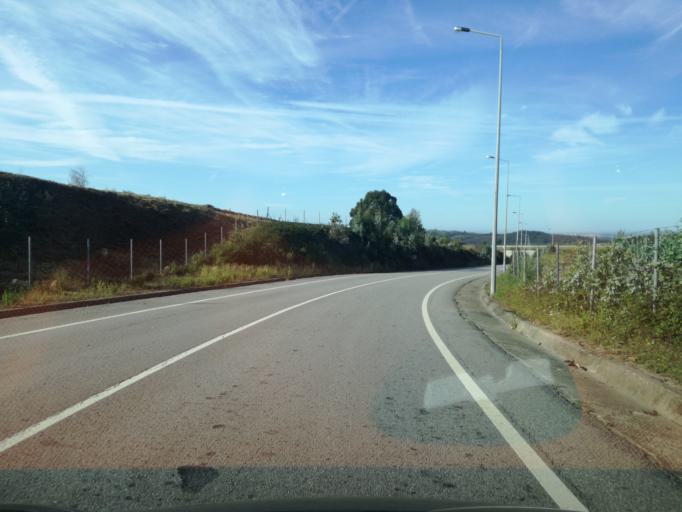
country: PT
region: Porto
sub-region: Trofa
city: Sao Romao do Coronado
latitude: 41.2858
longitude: -8.5160
